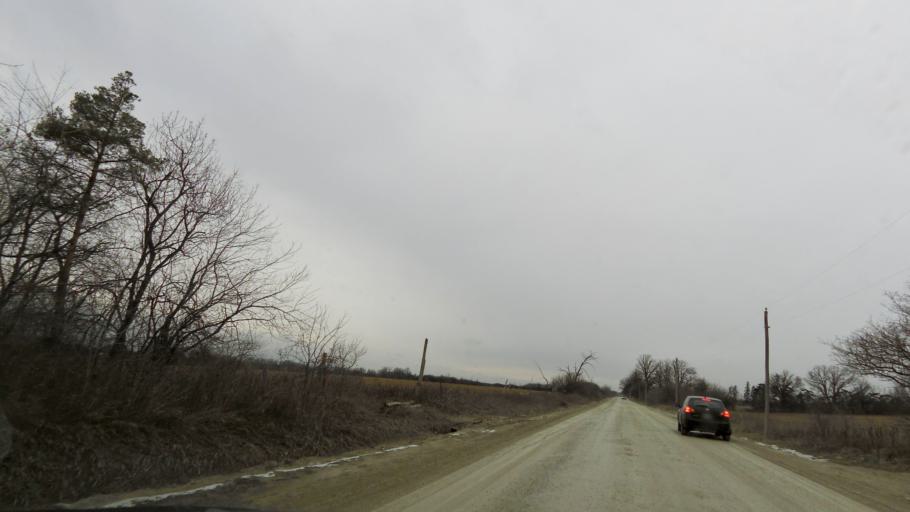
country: CA
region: Ontario
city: Vaughan
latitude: 43.8089
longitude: -79.6435
